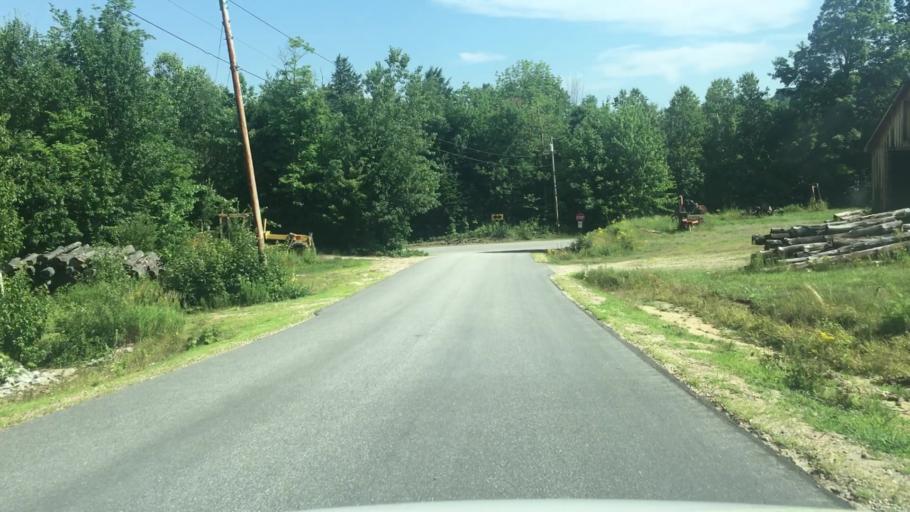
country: US
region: Maine
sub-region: Oxford County
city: West Paris
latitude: 44.3251
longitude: -70.5089
